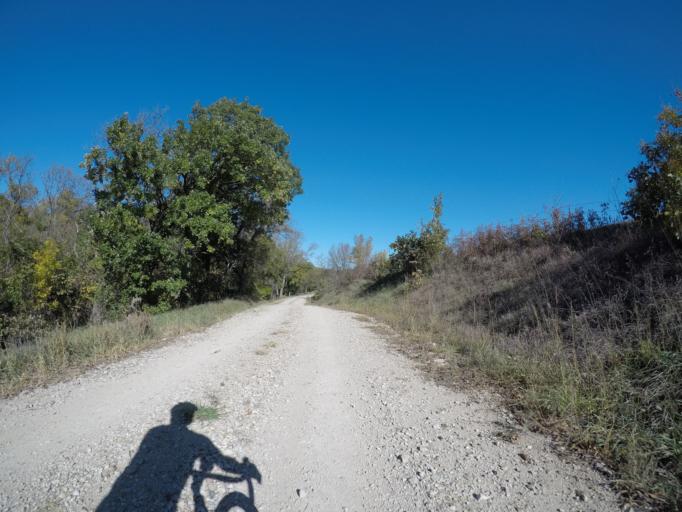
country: US
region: Kansas
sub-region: Wabaunsee County
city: Alma
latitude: 38.9343
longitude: -96.4008
